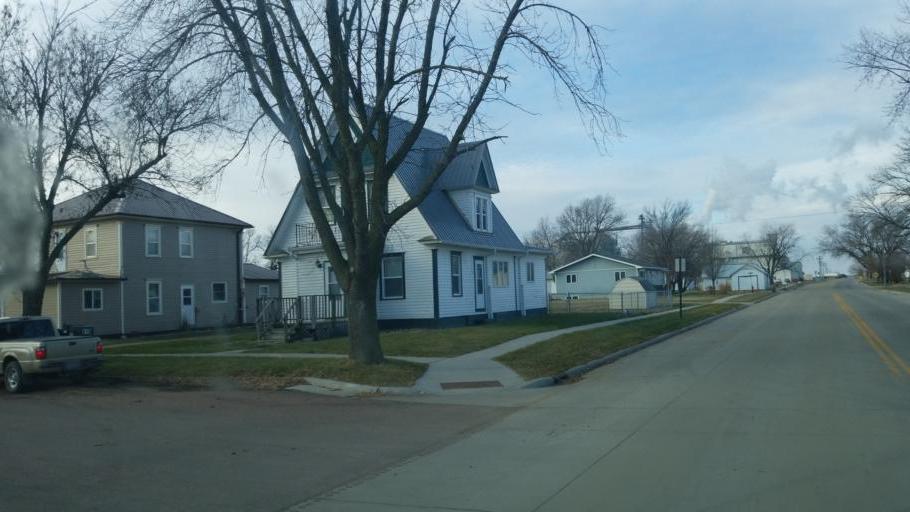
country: US
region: South Dakota
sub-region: Hutchinson County
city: Olivet
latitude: 43.1476
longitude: -97.7216
